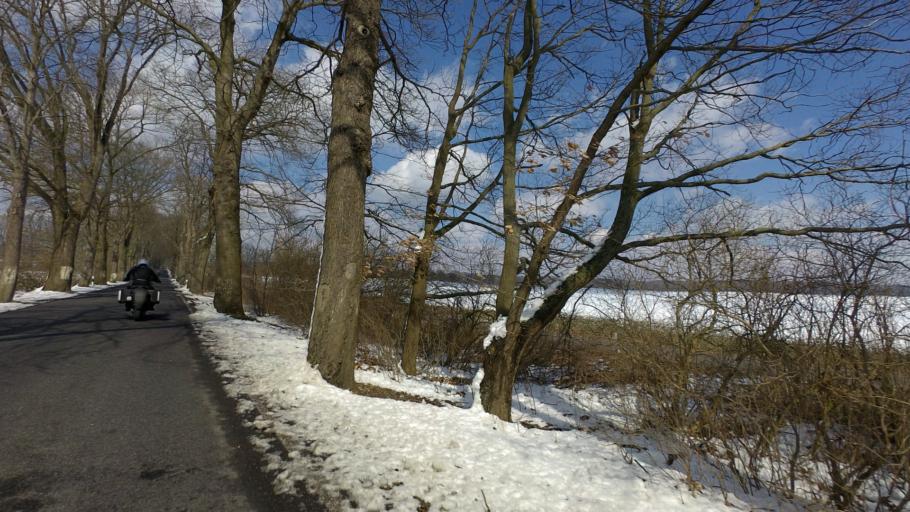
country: DE
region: Brandenburg
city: Joachimsthal
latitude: 52.9009
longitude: 13.7124
